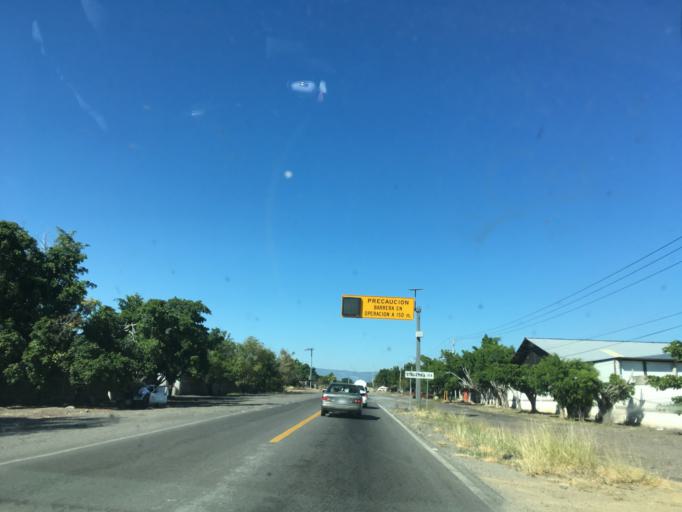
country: MX
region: Michoacan
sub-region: Gabriel Zamora
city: Lombardia
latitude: 19.0951
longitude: -102.0579
